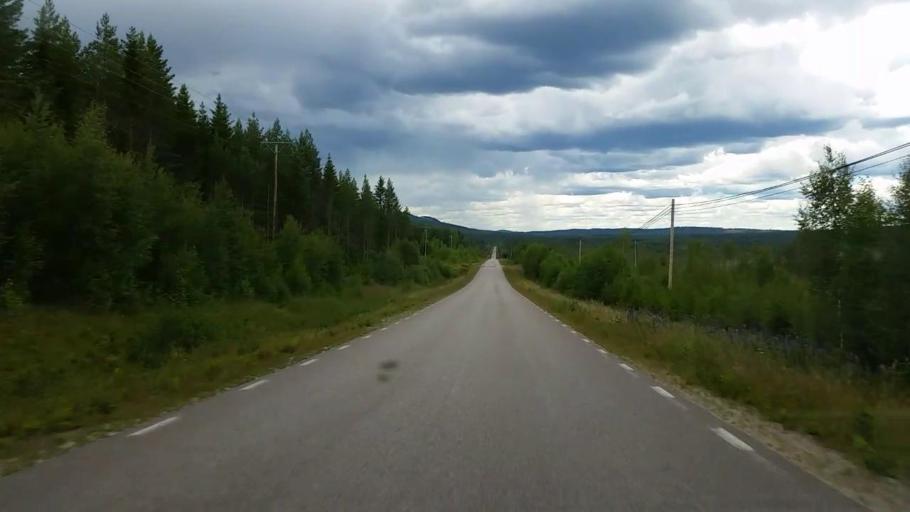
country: SE
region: Gaevleborg
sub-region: Ovanakers Kommun
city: Edsbyn
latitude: 61.4336
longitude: 15.8978
